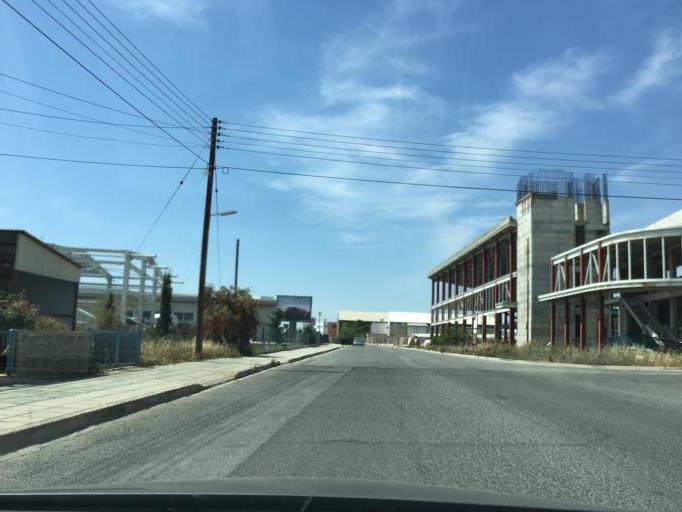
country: CY
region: Limassol
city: Mouttagiaka
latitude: 34.7033
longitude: 33.0690
